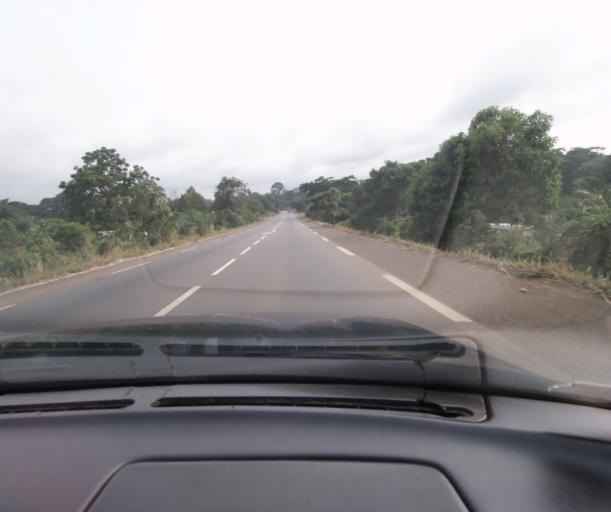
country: CM
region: Centre
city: Obala
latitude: 4.0997
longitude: 11.5375
